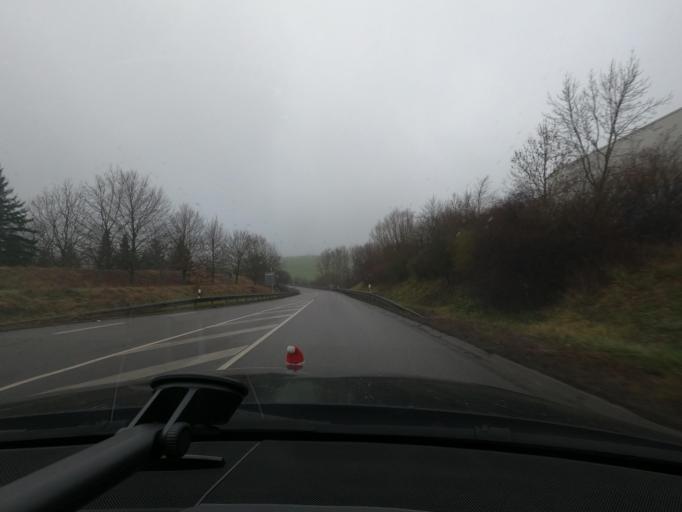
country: DE
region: Thuringia
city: Heilbad Heiligenstadt
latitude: 51.3850
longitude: 10.1548
